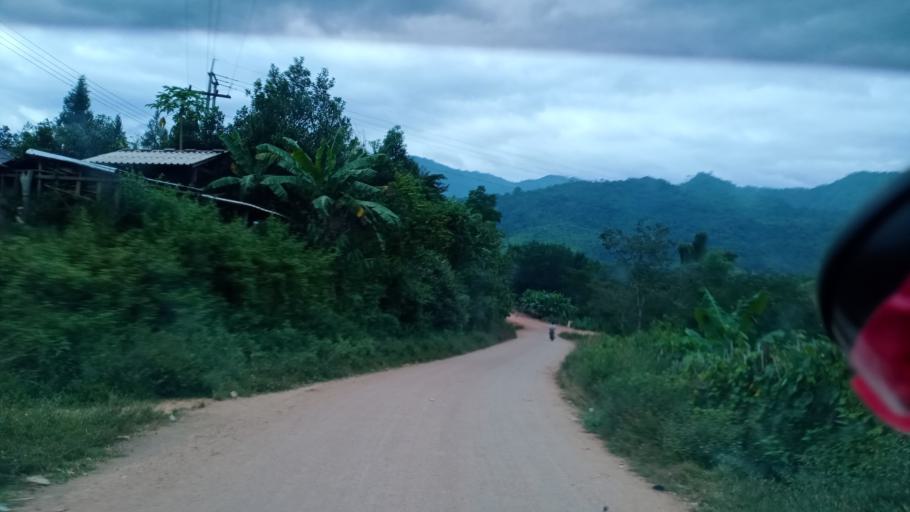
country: TH
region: Changwat Bueng Kan
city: Pak Khat
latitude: 18.7140
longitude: 103.2114
